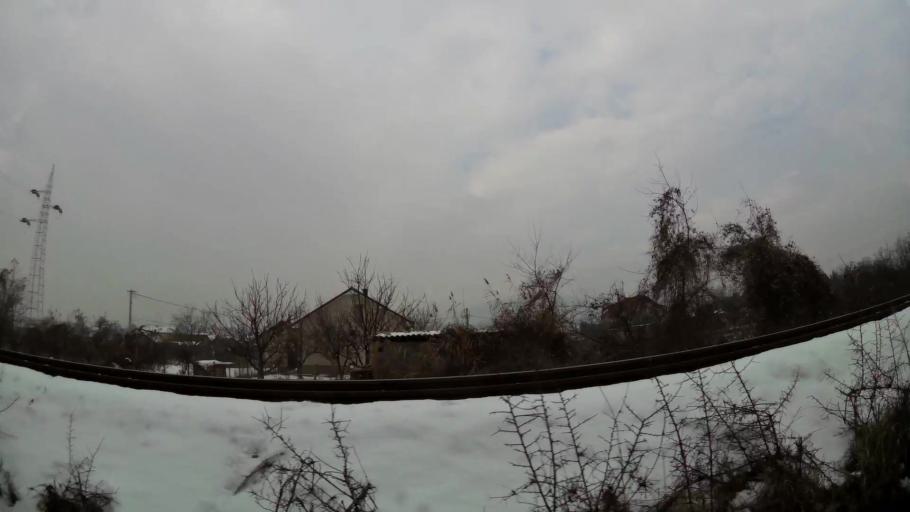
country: MK
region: Saraj
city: Saraj
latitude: 42.0398
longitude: 21.3522
